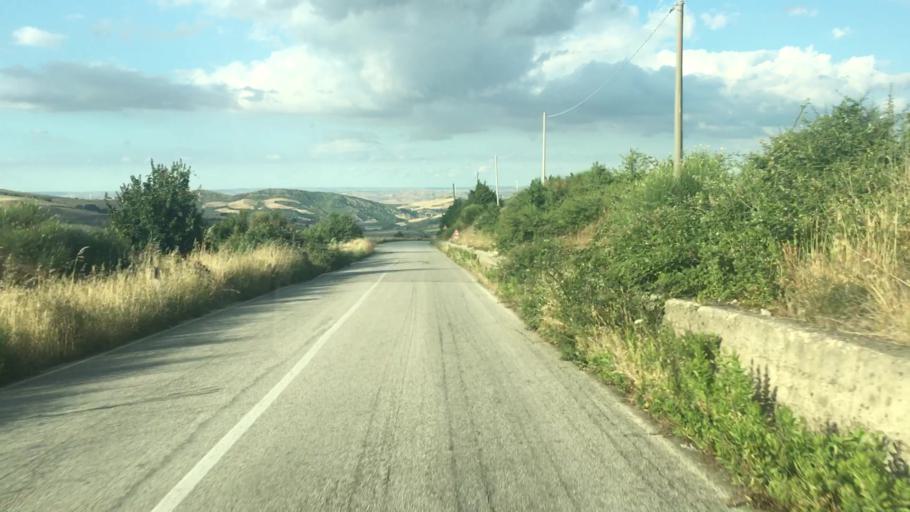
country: IT
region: Basilicate
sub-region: Provincia di Potenza
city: Tolve
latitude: 40.6974
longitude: 15.9940
